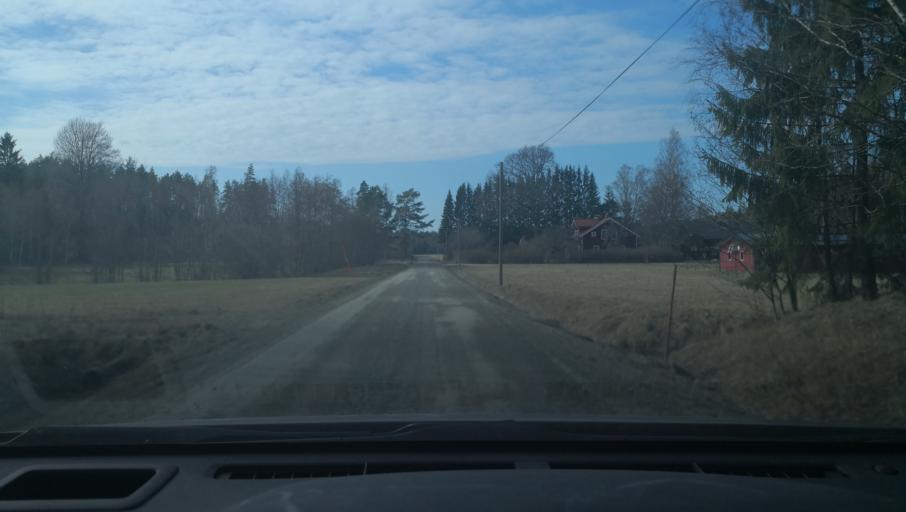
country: SE
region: Uppsala
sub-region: Heby Kommun
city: Heby
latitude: 59.8463
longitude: 16.8943
